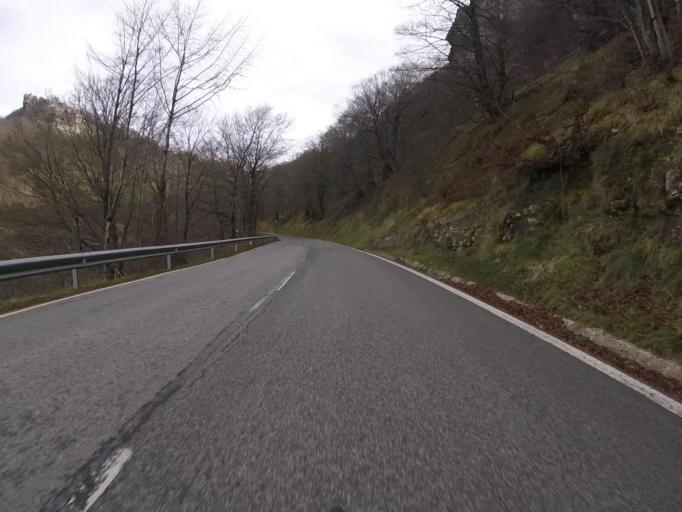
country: ES
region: Navarre
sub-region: Provincia de Navarra
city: Olazagutia
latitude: 42.8600
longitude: -2.1864
